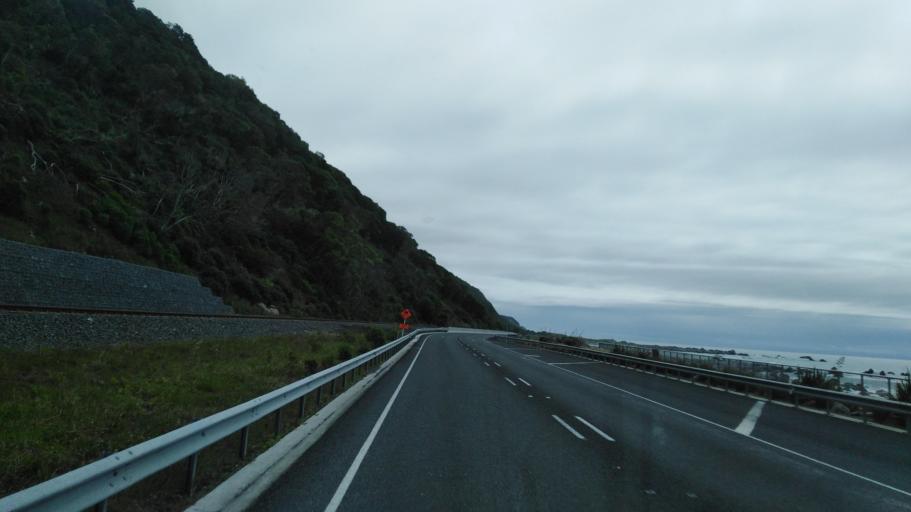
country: NZ
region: Canterbury
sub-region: Kaikoura District
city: Kaikoura
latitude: -42.2427
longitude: 173.8359
